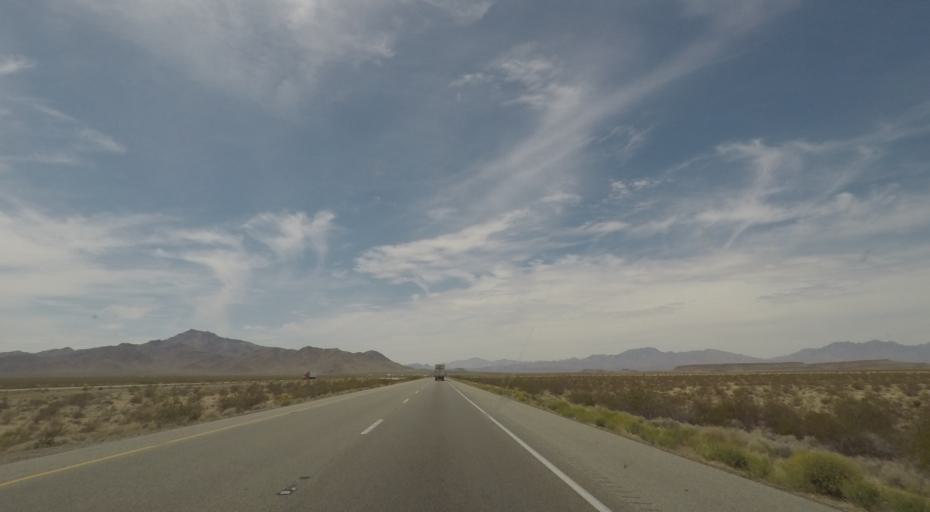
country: US
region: California
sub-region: San Bernardino County
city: Needles
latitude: 34.8041
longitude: -115.2852
